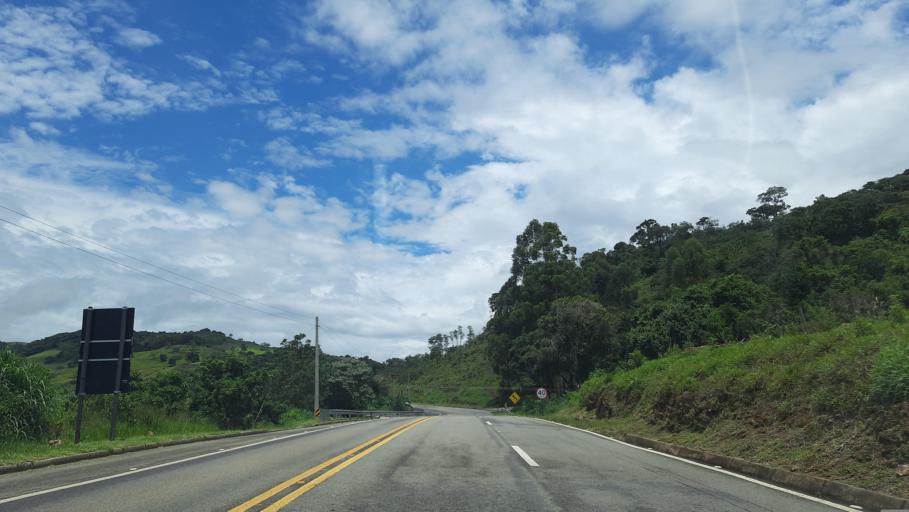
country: BR
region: Sao Paulo
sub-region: Vargem Grande Do Sul
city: Vargem Grande do Sul
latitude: -21.8323
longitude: -46.7585
